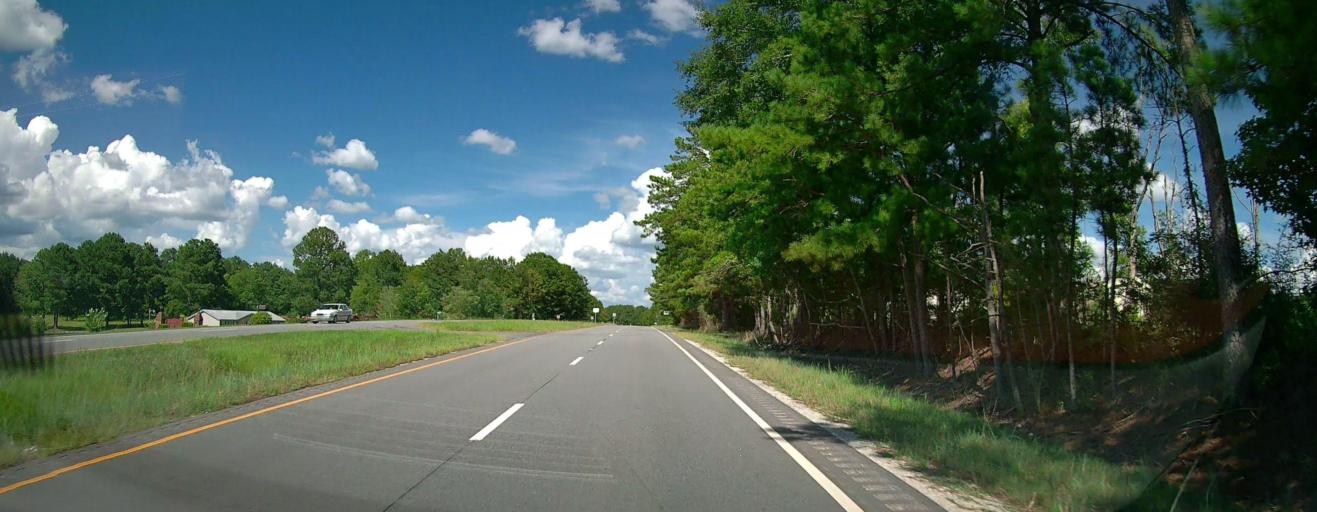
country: US
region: Alabama
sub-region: Macon County
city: Tuskegee
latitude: 32.3823
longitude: -85.7682
